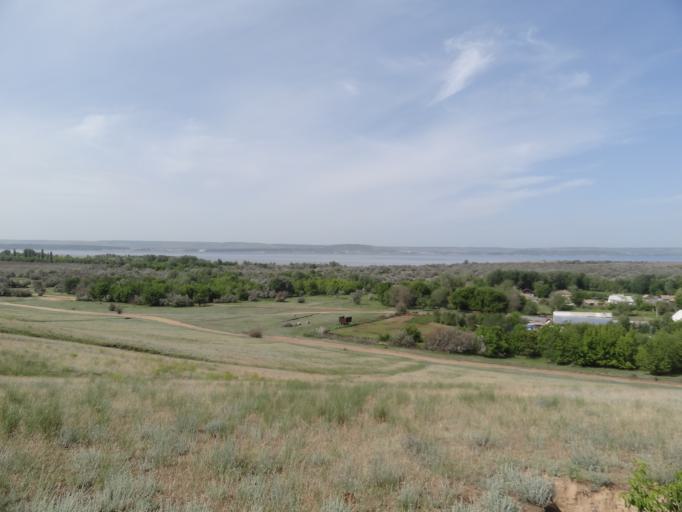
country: RU
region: Saratov
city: Krasnoarmeysk
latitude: 51.1547
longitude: 45.9331
